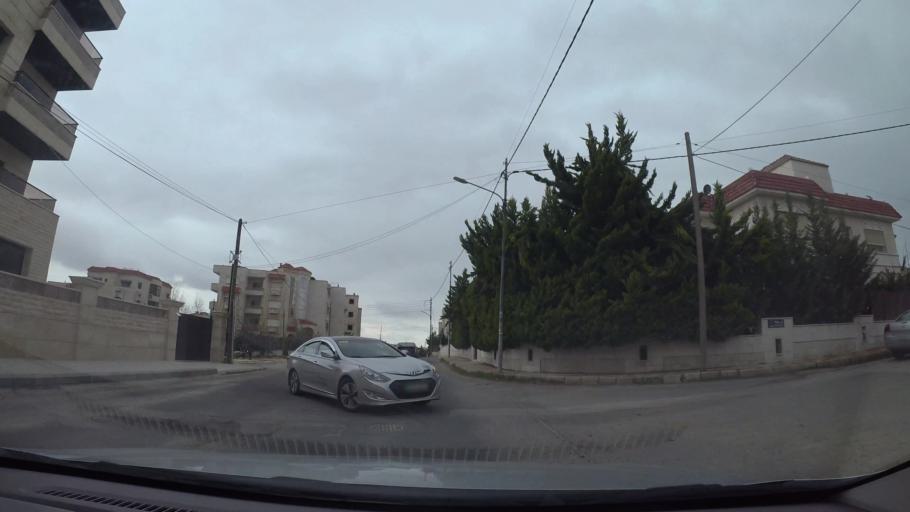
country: JO
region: Amman
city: Al Jubayhah
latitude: 31.9953
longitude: 35.8455
